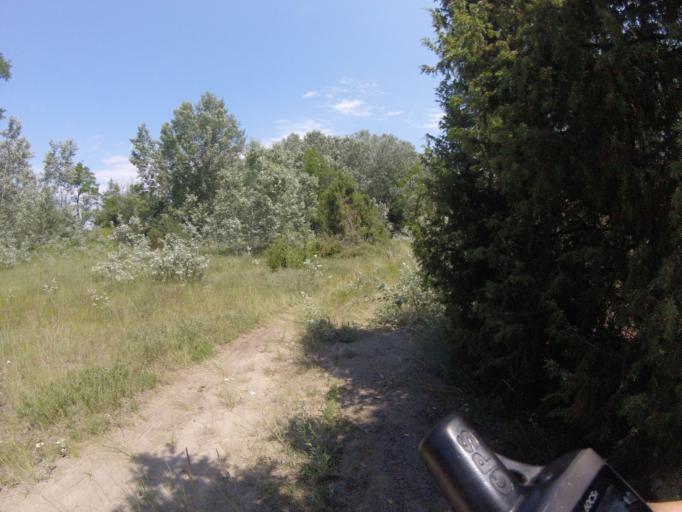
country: HU
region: Bacs-Kiskun
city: Jaszszentlaszlo
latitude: 46.6100
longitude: 19.7110
